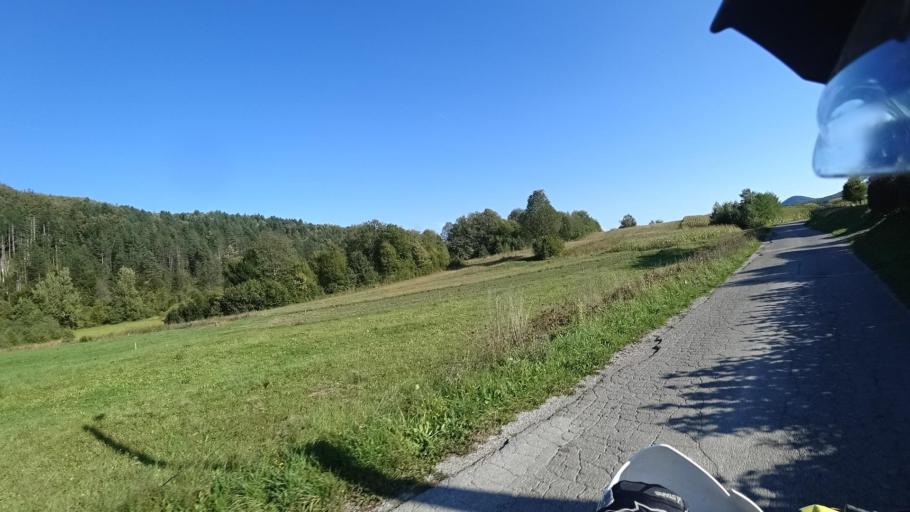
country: HR
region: Karlovacka
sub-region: Grad Ogulin
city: Ogulin
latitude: 45.2909
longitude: 15.1536
